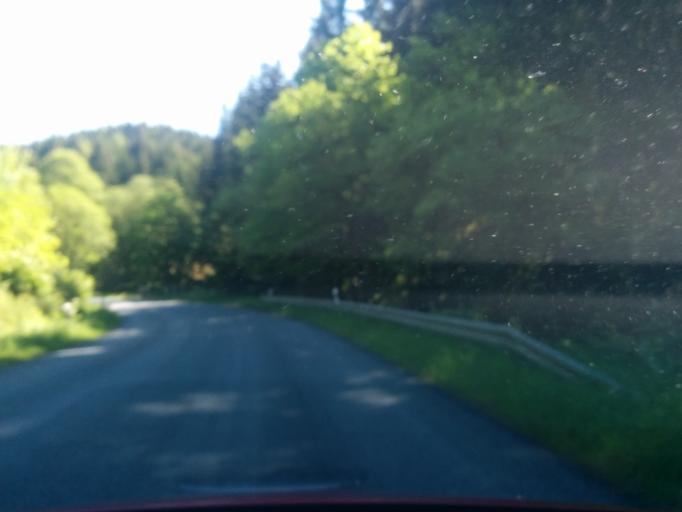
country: DE
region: Lower Saxony
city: Sankt Andreasberg
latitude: 51.6959
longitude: 10.5087
